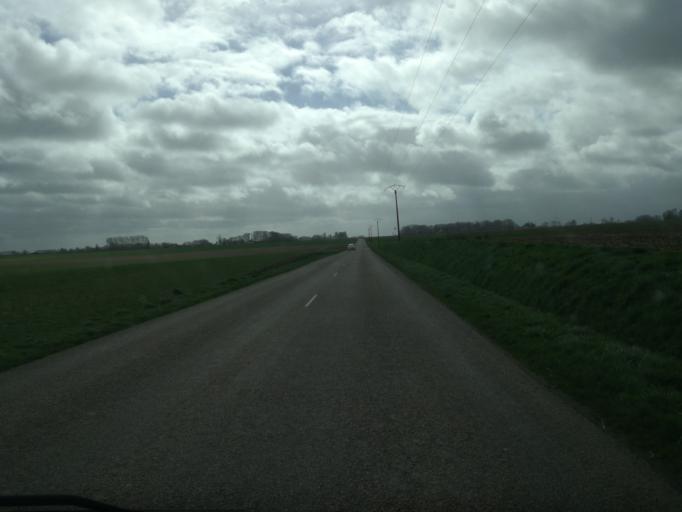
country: FR
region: Haute-Normandie
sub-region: Departement de la Seine-Maritime
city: Valliquerville
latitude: 49.6072
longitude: 0.6666
